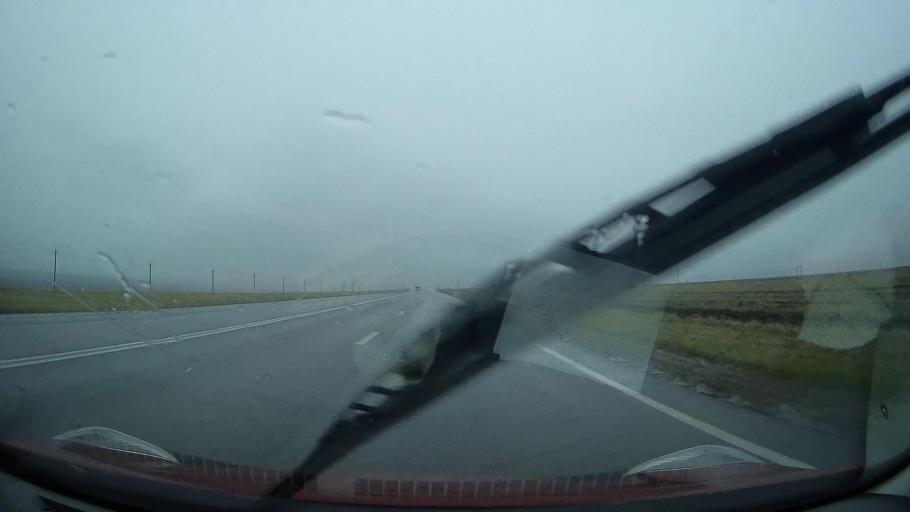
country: RU
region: Stavropol'skiy
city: Kursavka
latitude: 44.5806
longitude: 42.2449
